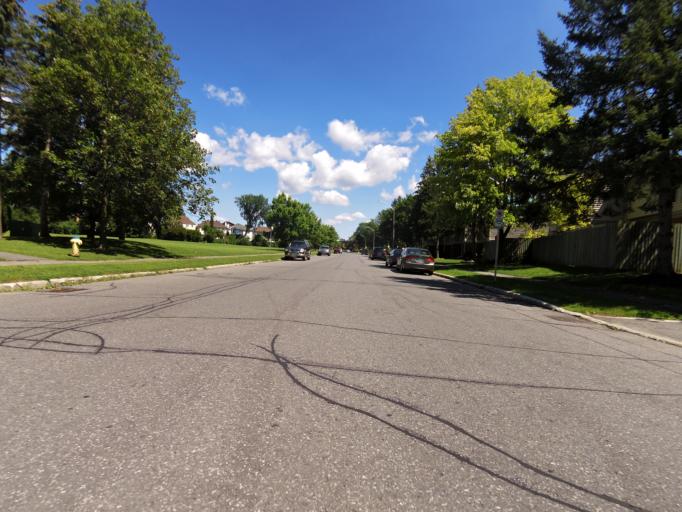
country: CA
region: Ontario
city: Ottawa
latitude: 45.3466
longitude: -75.6662
